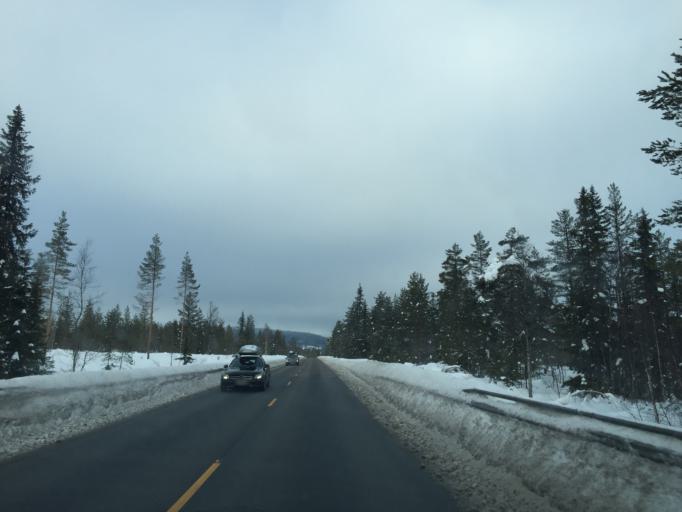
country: NO
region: Hedmark
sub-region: Trysil
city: Innbygda
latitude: 61.1494
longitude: 12.1297
